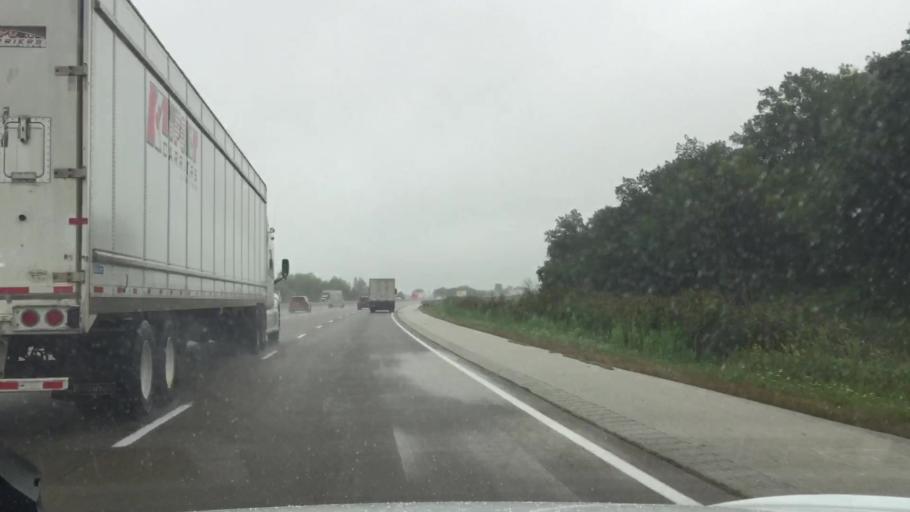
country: US
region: Michigan
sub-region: Wayne County
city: Grosse Pointe Farms
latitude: 42.2417
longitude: -82.5781
